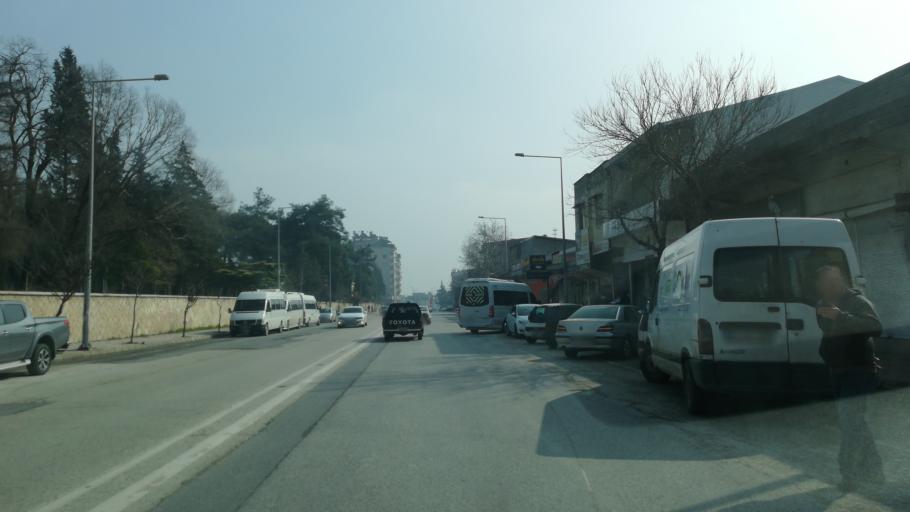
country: TR
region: Kahramanmaras
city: Kahramanmaras
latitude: 37.5739
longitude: 36.9384
